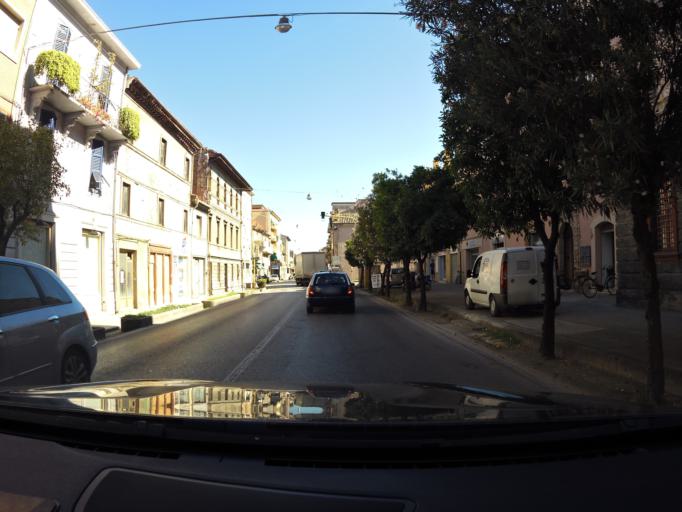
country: IT
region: The Marches
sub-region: Province of Fermo
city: Porto San Giorgio
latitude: 43.1792
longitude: 13.7936
